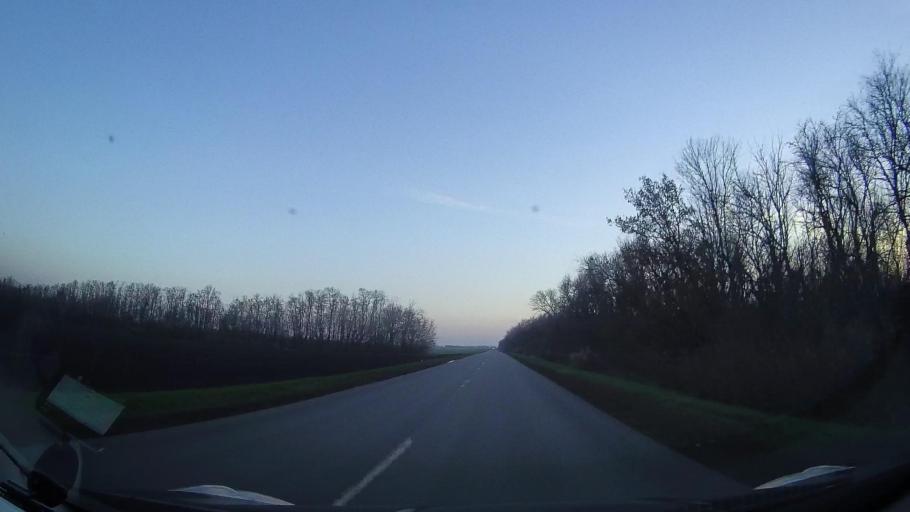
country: RU
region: Rostov
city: Zernograd
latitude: 46.9901
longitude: 40.3915
